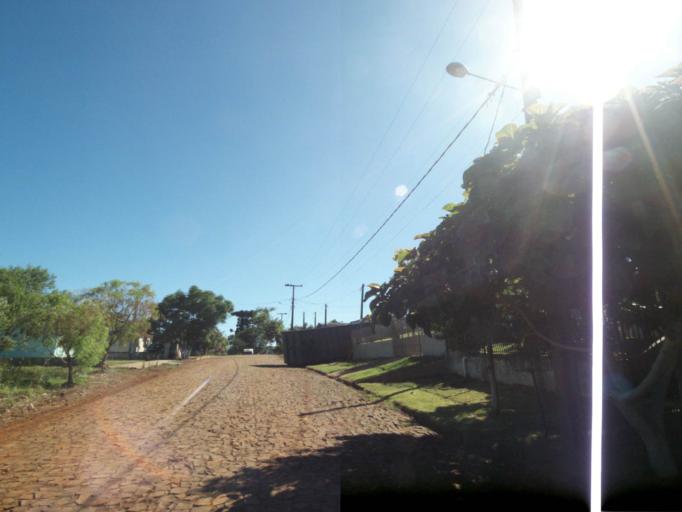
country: BR
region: Parana
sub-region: Pato Branco
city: Pato Branco
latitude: -26.2588
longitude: -52.7776
